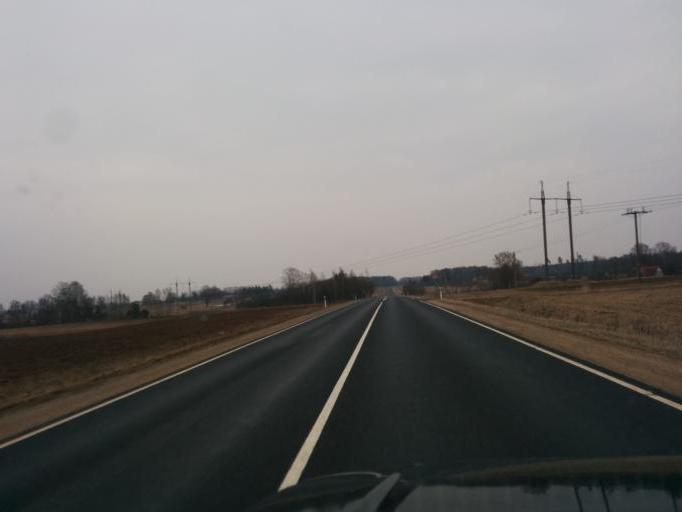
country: LV
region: Salaspils
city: Salaspils
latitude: 56.8262
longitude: 24.3524
